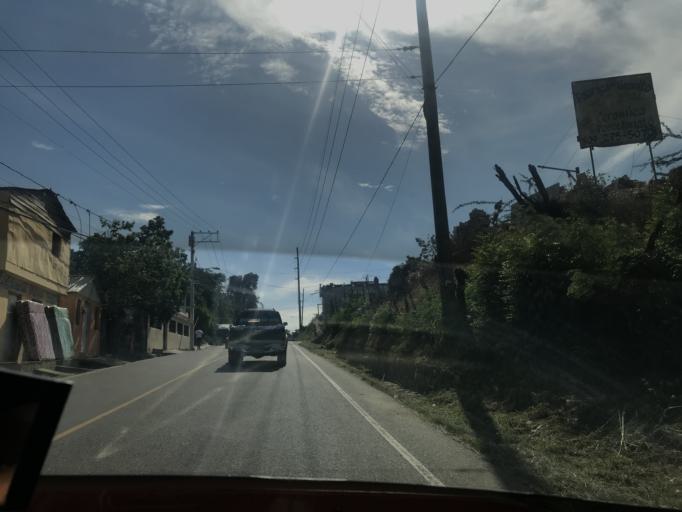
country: DO
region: Santiago
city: Santiago de los Caballeros
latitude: 19.4516
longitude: -70.7556
